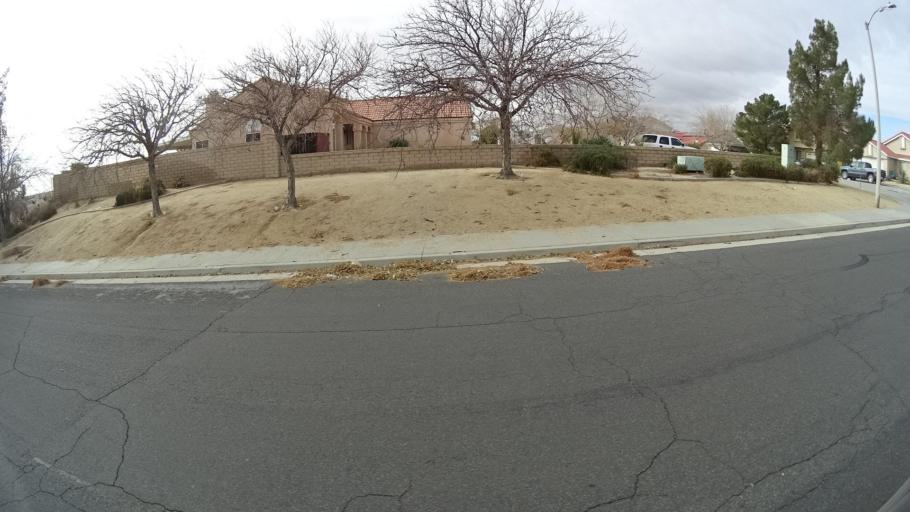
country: US
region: California
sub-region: Kern County
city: Rosamond
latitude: 34.8712
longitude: -118.1495
